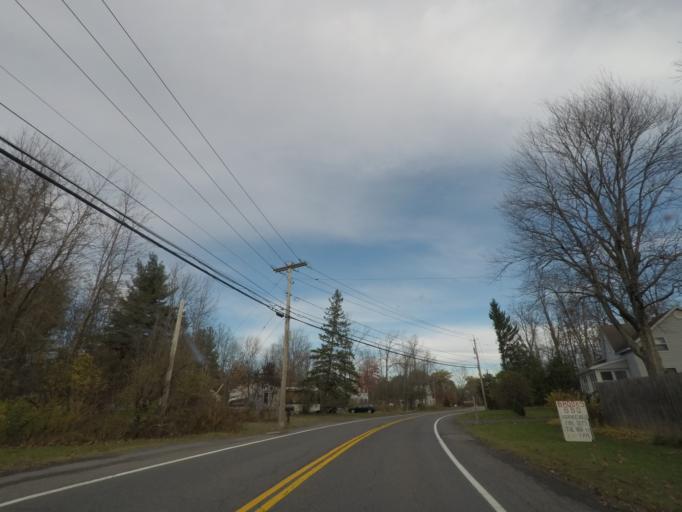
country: US
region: New York
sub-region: Albany County
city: Voorheesville
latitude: 42.6439
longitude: -73.9603
